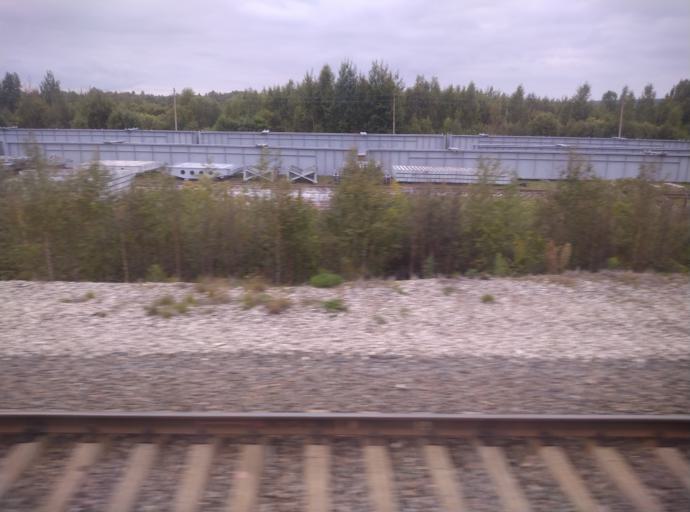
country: RU
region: Kostroma
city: Kosmynino
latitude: 57.5923
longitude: 40.7682
